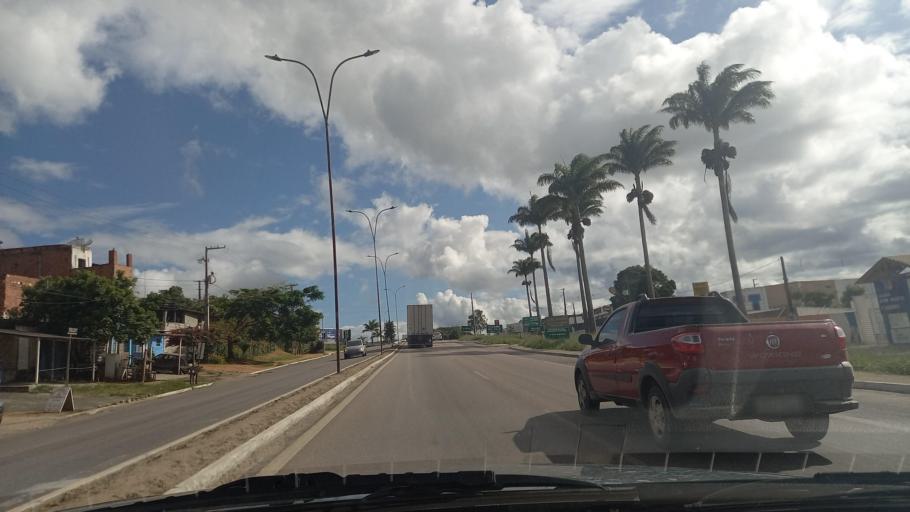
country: BR
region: Pernambuco
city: Garanhuns
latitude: -8.8750
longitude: -36.4712
